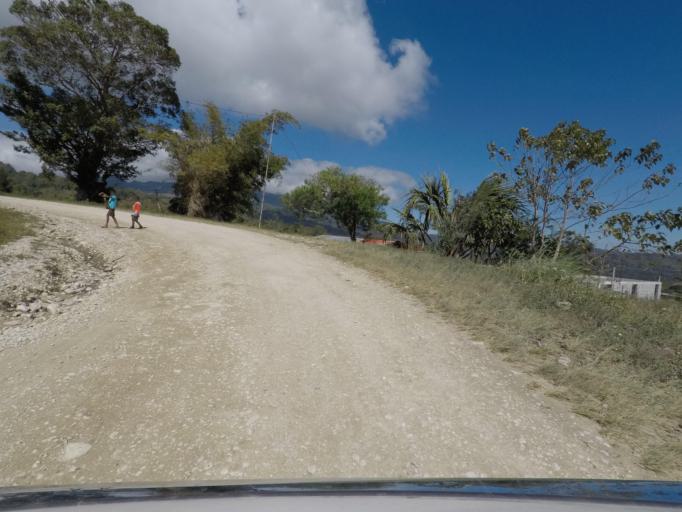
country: TL
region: Baucau
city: Venilale
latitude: -8.6767
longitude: 126.3709
